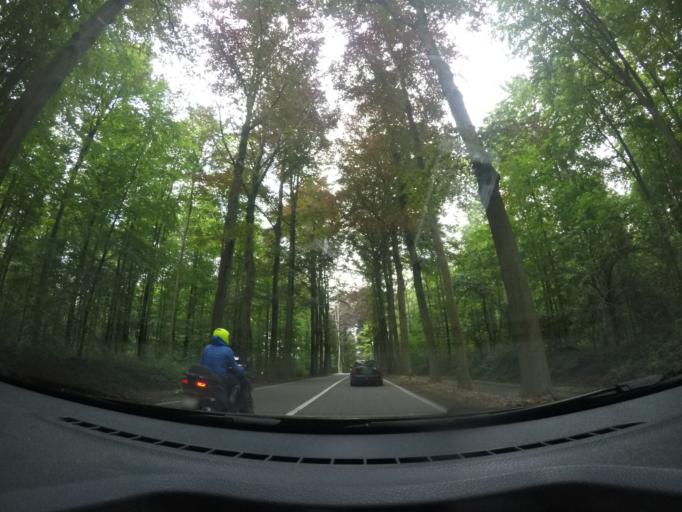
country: BE
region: Flanders
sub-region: Provincie Vlaams-Brabant
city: Sint-Genesius-Rode
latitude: 50.7817
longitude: 4.3879
